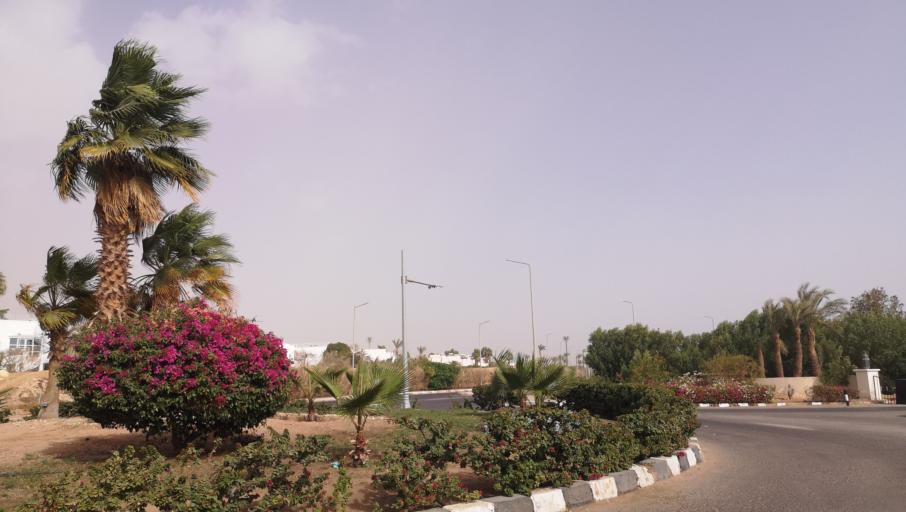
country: EG
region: South Sinai
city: Sharm el-Sheikh
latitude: 27.8651
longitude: 34.3161
